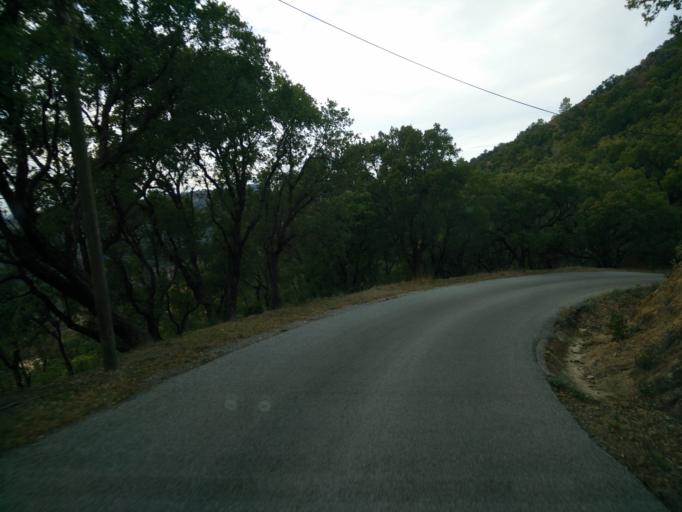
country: FR
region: Provence-Alpes-Cote d'Azur
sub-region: Departement du Var
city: Sainte-Maxime
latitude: 43.3642
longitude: 6.6073
